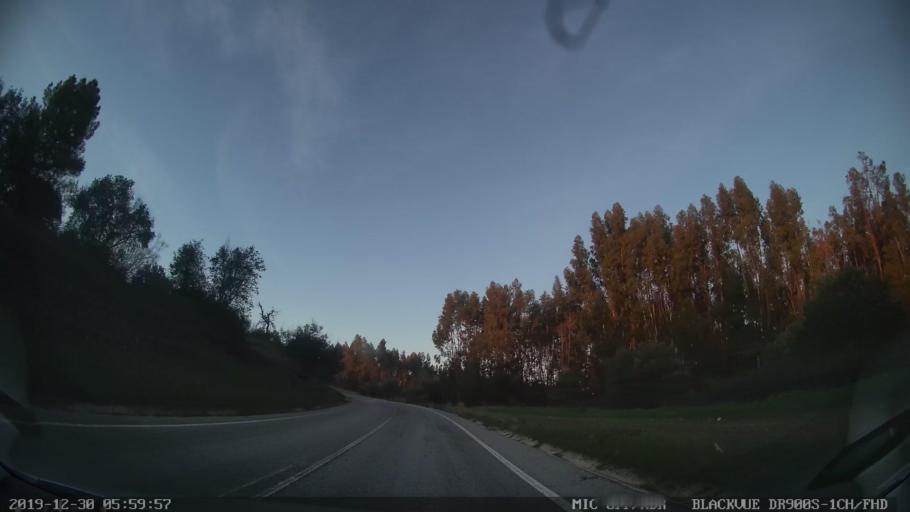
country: PT
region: Castelo Branco
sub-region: Idanha-A-Nova
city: Idanha-a-Nova
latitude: 40.0483
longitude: -7.2437
